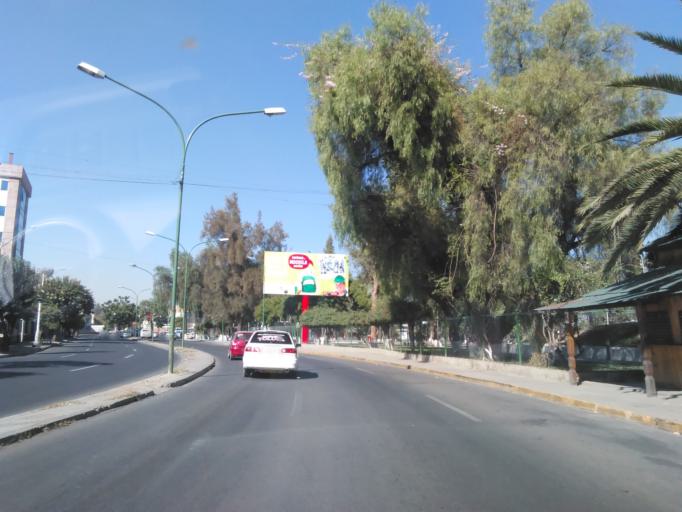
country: BO
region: Cochabamba
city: Cochabamba
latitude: -17.3849
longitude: -66.1625
